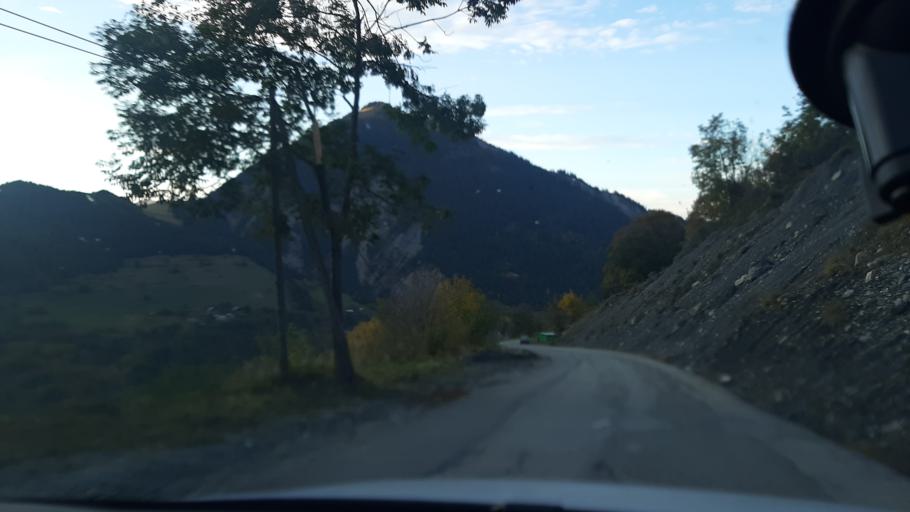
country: FR
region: Rhone-Alpes
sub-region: Departement de la Savoie
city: Villargondran
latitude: 45.1918
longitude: 6.3116
